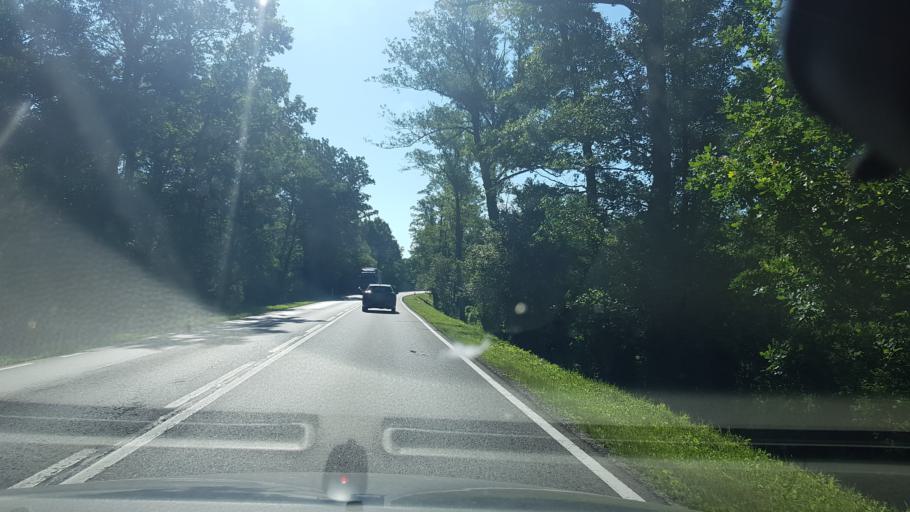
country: PL
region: Masovian Voivodeship
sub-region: Powiat wyszkowski
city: Branszczyk
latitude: 52.5561
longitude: 21.5921
